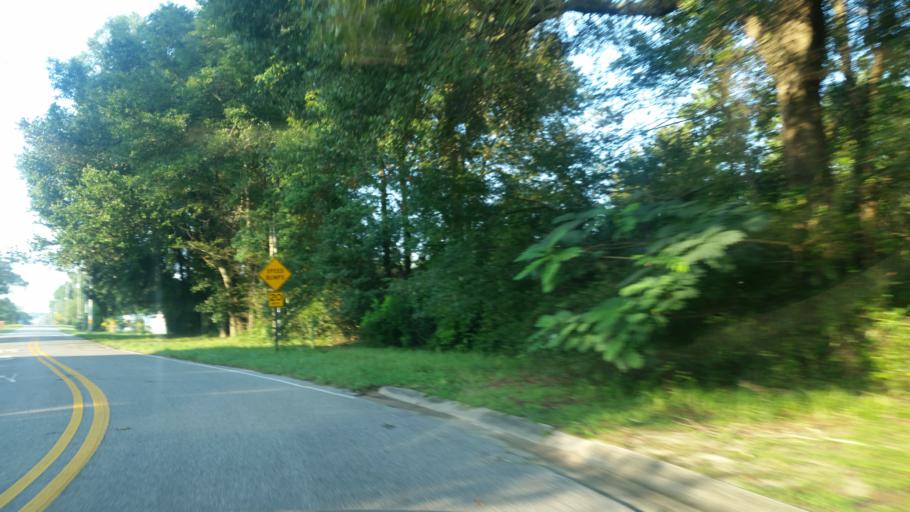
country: US
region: Florida
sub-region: Escambia County
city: Ferry Pass
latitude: 30.5397
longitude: -87.2265
